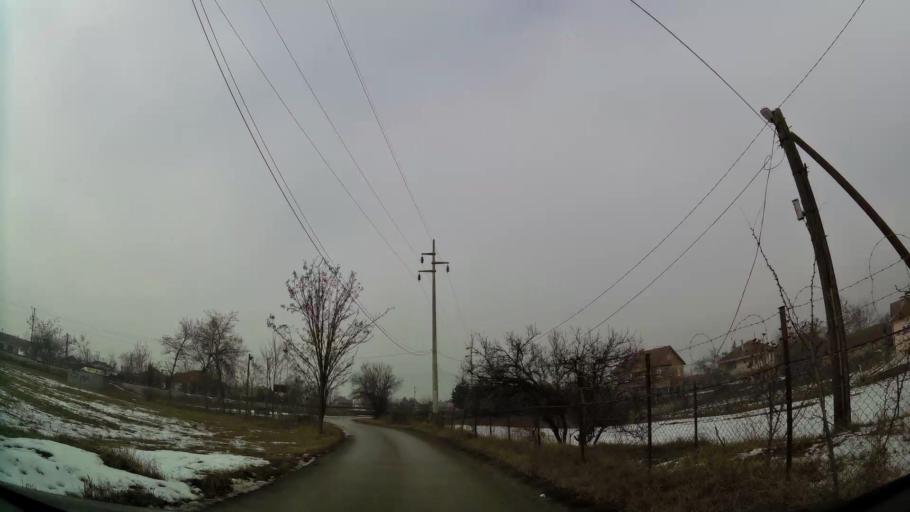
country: MK
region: Ilinden
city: Ilinden
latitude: 41.9964
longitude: 21.5617
